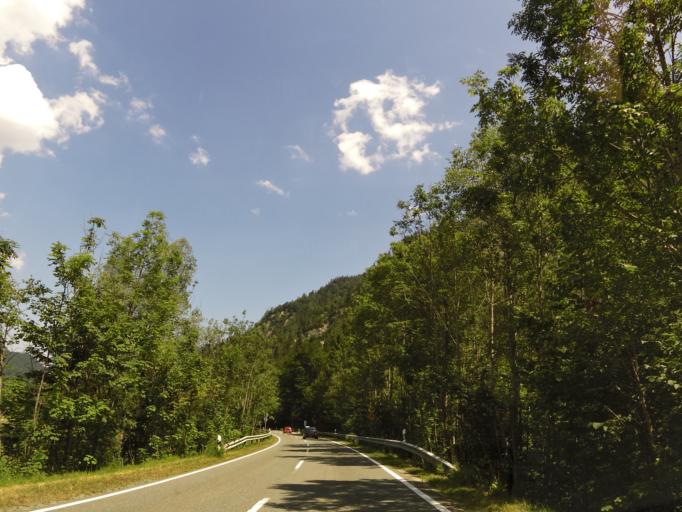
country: DE
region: Bavaria
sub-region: Upper Bavaria
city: Ruhpolding
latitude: 47.6874
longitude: 12.5841
